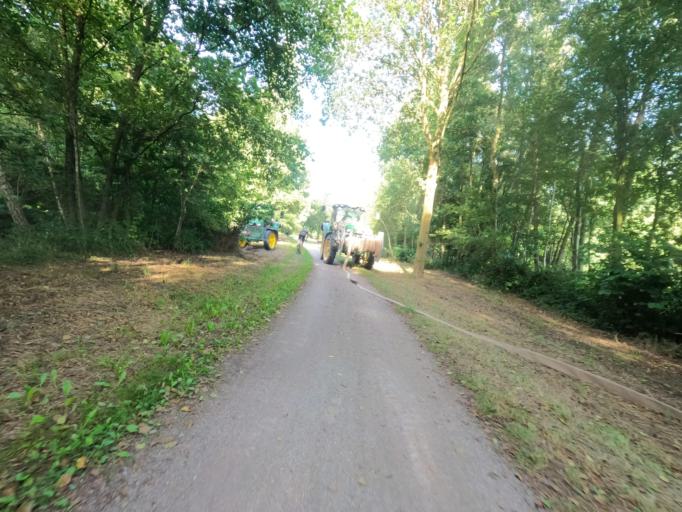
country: DE
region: North Rhine-Westphalia
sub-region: Regierungsbezirk Dusseldorf
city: Bruggen
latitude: 51.2357
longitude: 6.1578
